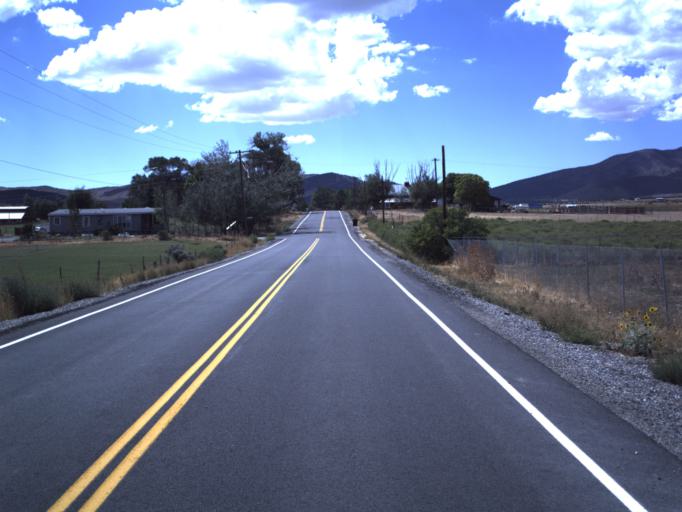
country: US
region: Utah
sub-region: Tooele County
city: Grantsville
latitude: 40.3383
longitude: -112.4780
